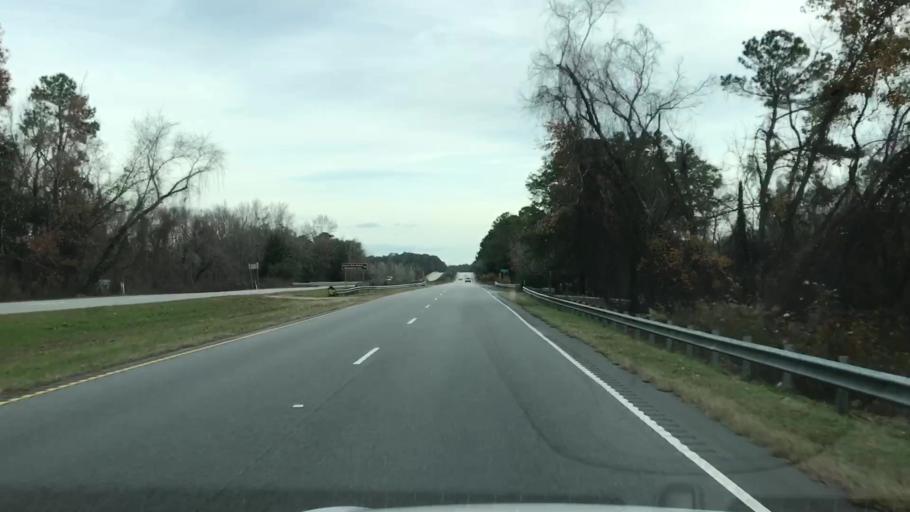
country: US
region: South Carolina
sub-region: Georgetown County
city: Georgetown
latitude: 33.2043
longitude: -79.3883
